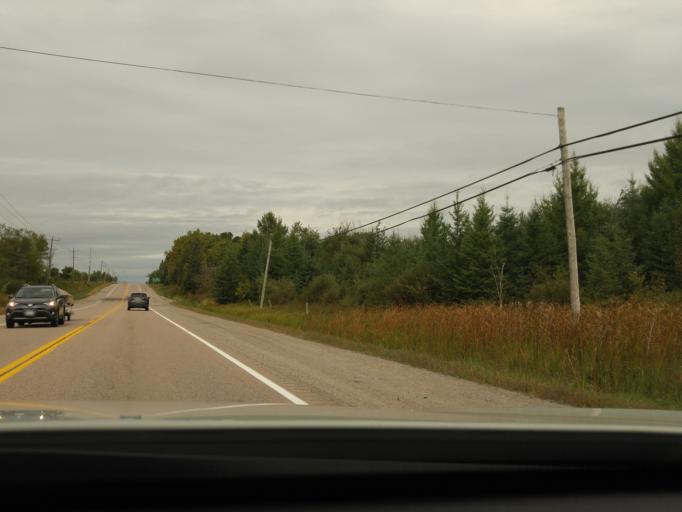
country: CA
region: Ontario
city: Renfrew
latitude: 45.5751
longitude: -76.8160
